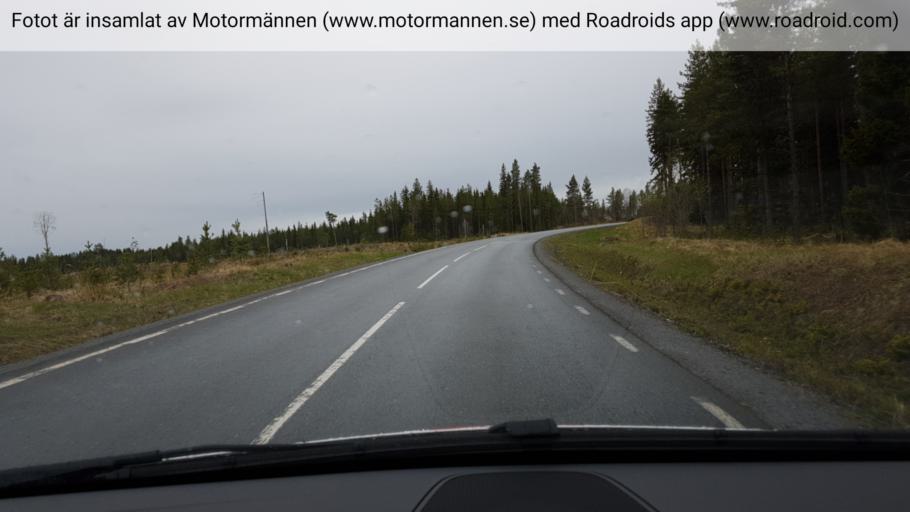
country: SE
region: Jaemtland
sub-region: Krokoms Kommun
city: Krokom
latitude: 63.2603
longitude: 14.4335
